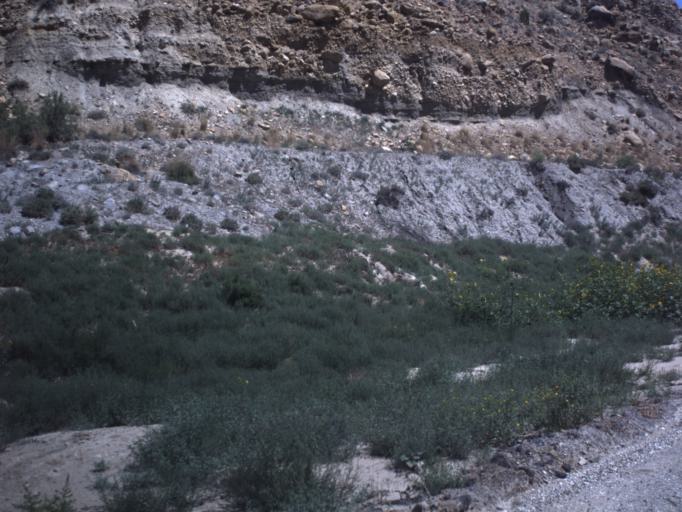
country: US
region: Utah
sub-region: Emery County
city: Orangeville
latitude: 39.2617
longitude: -111.1205
